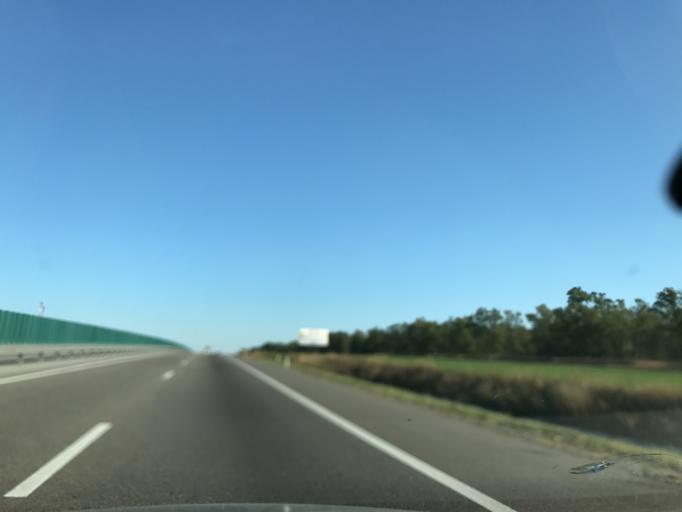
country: RU
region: Rostov
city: Glubokiy
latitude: 48.6204
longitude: 40.3556
